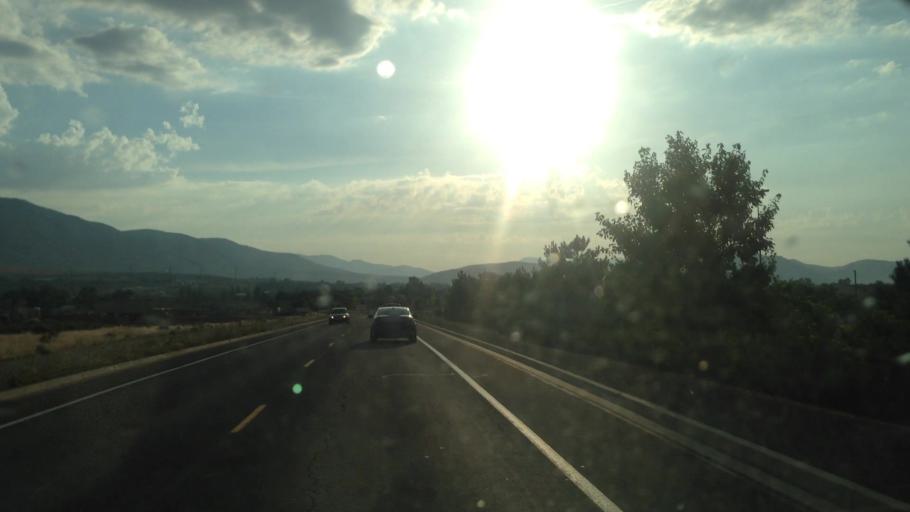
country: US
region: Nevada
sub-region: Washoe County
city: Lemmon Valley
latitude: 39.6216
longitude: -119.8652
